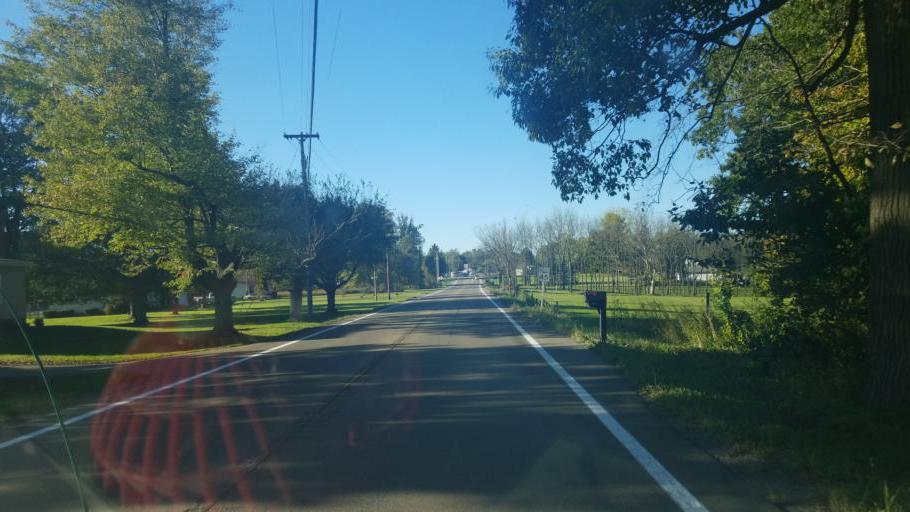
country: US
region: Ohio
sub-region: Columbiana County
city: New Waterford
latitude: 40.8389
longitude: -80.6474
